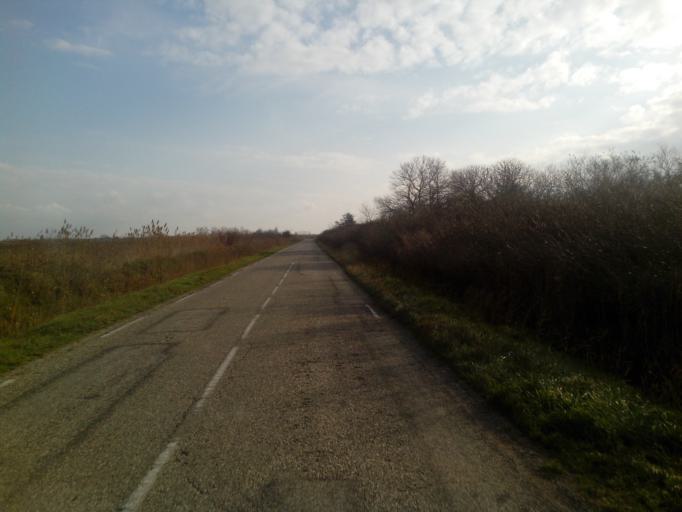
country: FR
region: Languedoc-Roussillon
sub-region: Departement du Gard
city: Saint-Gilles
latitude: 43.5939
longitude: 4.4917
